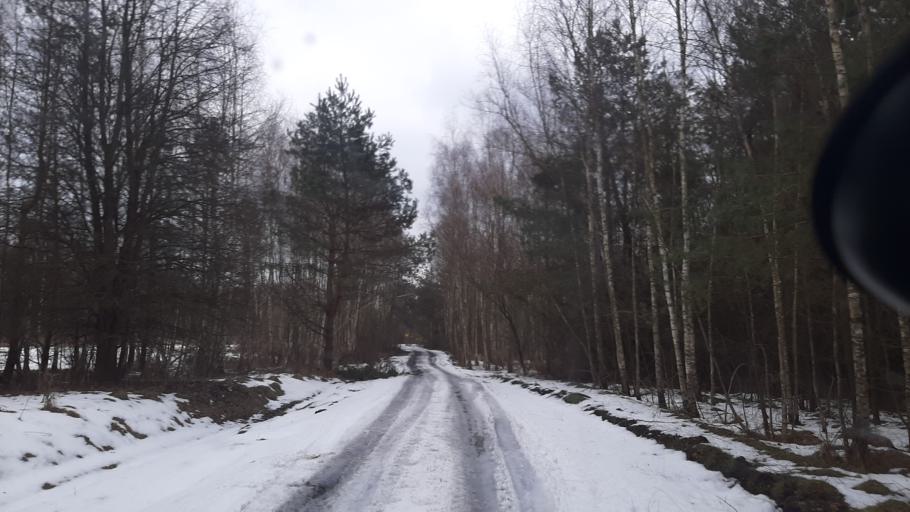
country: PL
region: Lublin Voivodeship
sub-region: Powiat wlodawski
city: Wlodawa
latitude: 51.5115
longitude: 23.6145
